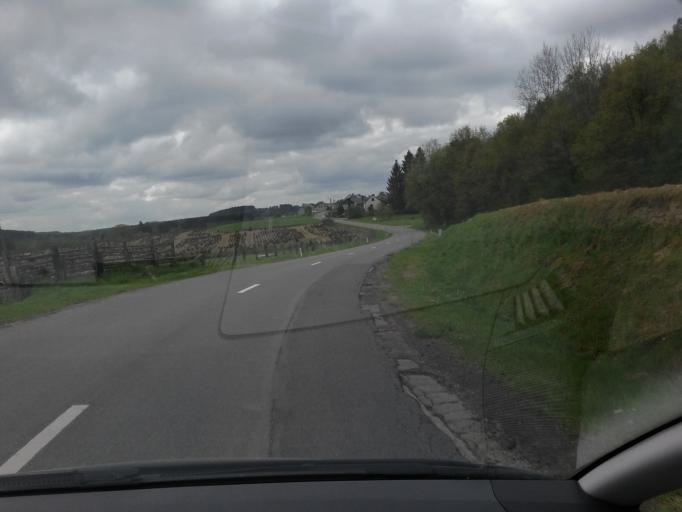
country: BE
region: Wallonia
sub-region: Province du Luxembourg
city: Bertrix
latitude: 49.8279
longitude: 5.3180
